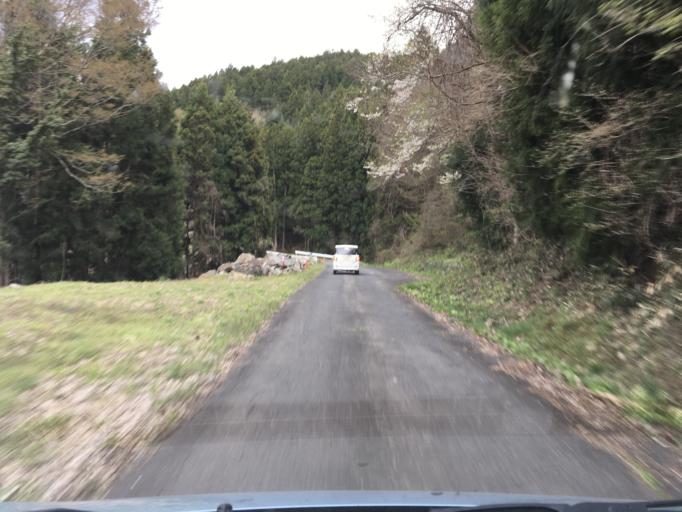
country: JP
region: Iwate
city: Ichinoseki
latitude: 38.9653
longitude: 141.2074
